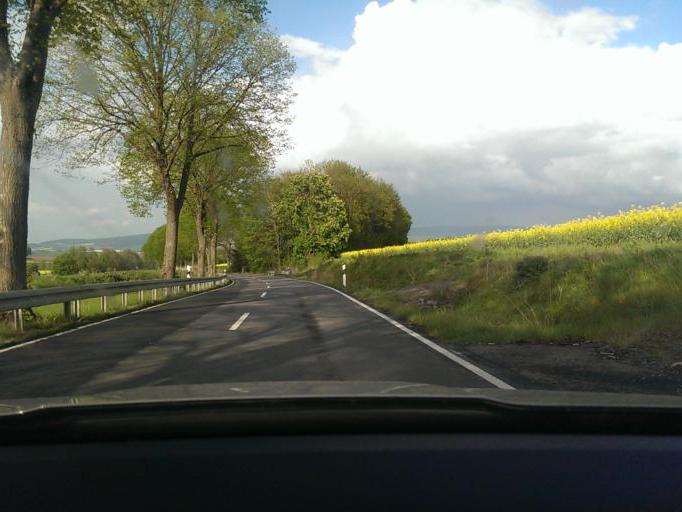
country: DE
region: Lower Saxony
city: Pohle
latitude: 52.2408
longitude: 9.2976
